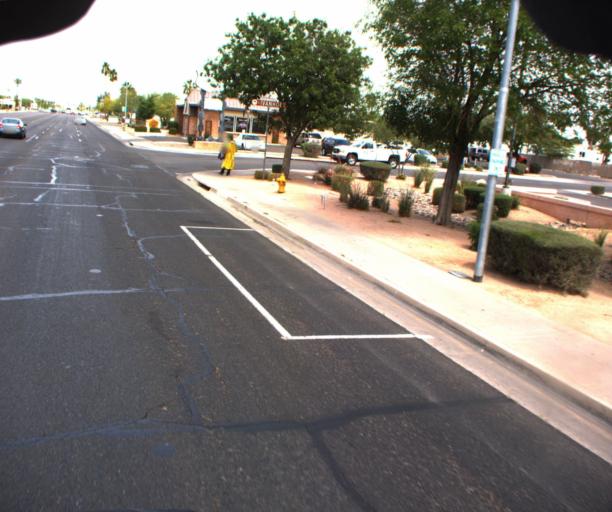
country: US
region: Arizona
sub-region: Maricopa County
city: Chandler
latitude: 33.3167
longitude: -111.8415
